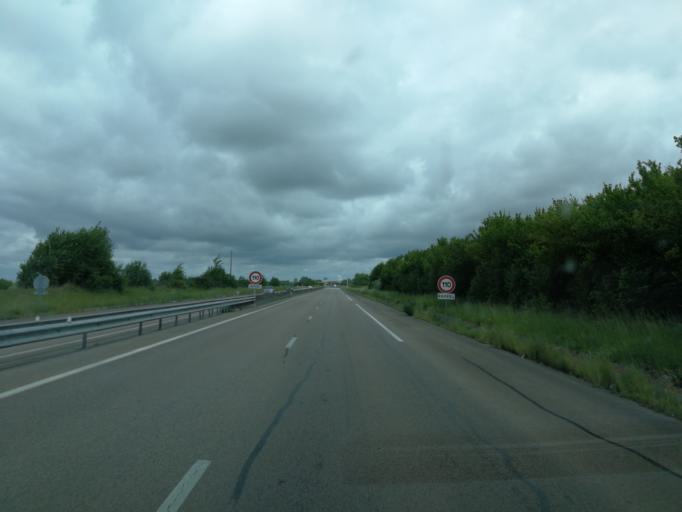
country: FR
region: Haute-Normandie
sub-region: Departement de l'Eure
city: Damville
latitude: 48.8799
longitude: 1.1744
